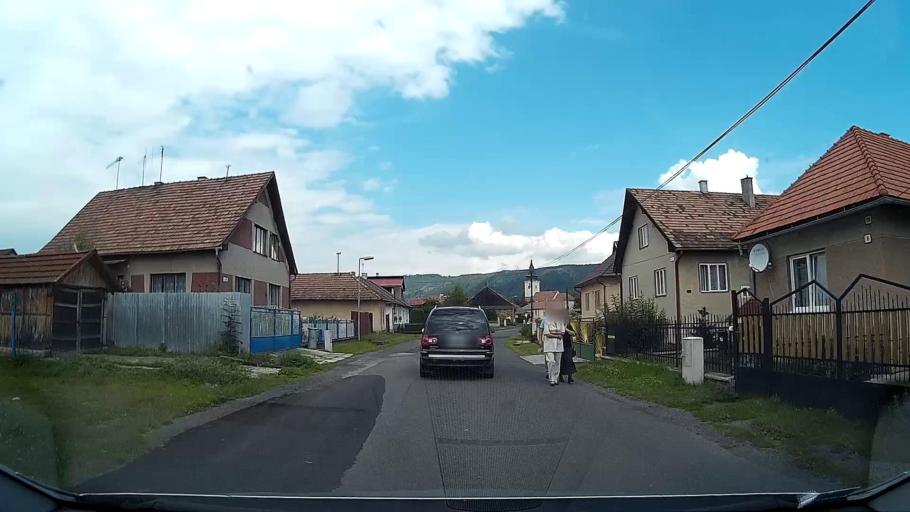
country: SK
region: Presovsky
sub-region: Okres Poprad
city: Poprad
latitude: 48.9925
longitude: 20.3610
